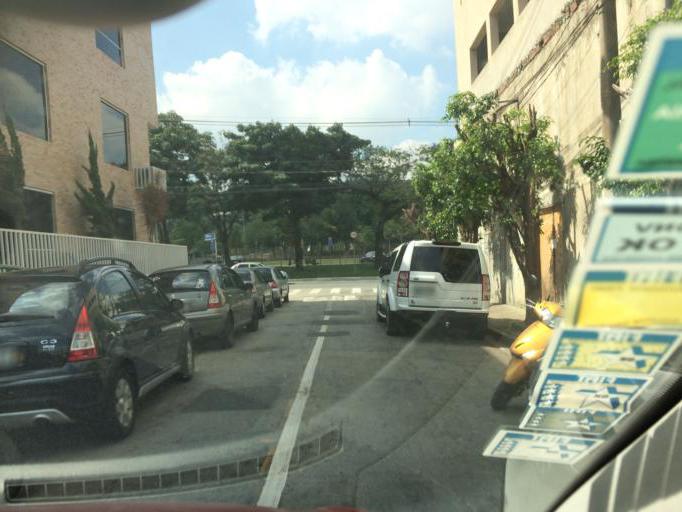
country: BR
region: Sao Paulo
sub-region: Guarulhos
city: Guarulhos
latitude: -23.4566
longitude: -46.5324
